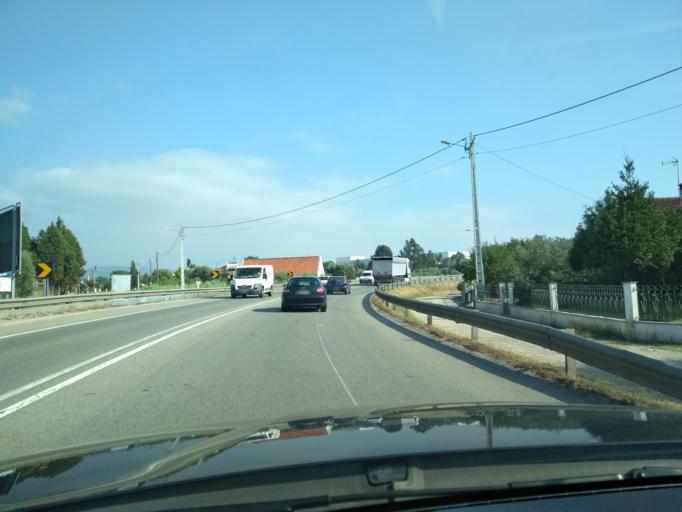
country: PT
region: Aveiro
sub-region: Mealhada
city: Mealhada
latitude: 40.3589
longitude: -8.4513
